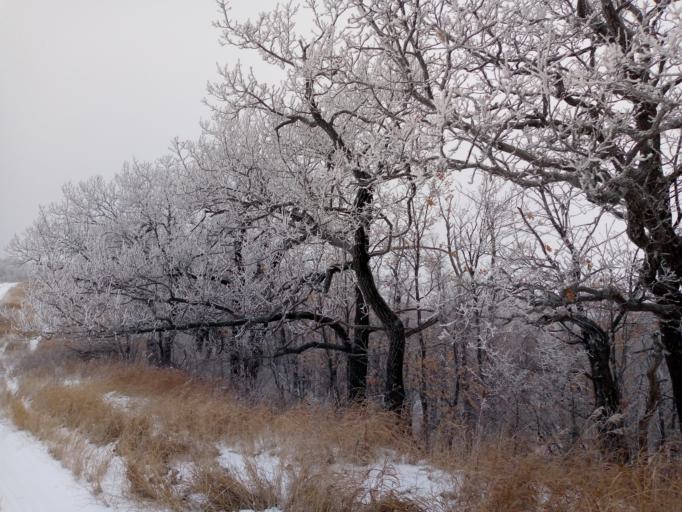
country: RU
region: Saratov
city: Krasnyy Oktyabr'
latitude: 51.3547
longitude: 45.7979
